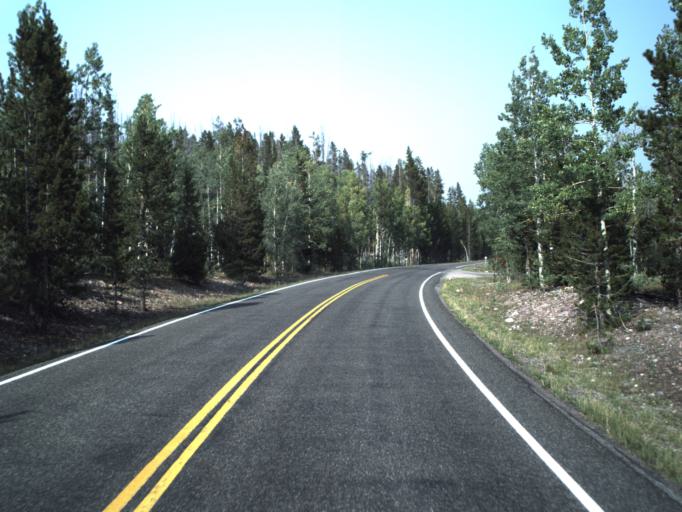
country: US
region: Utah
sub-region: Summit County
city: Oakley
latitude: 40.8055
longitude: -110.8787
